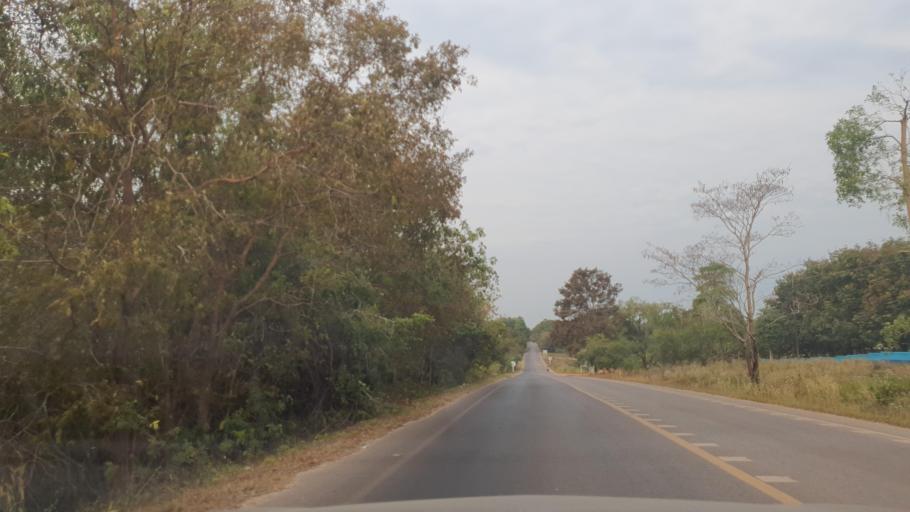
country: TH
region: Changwat Bueng Kan
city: Bung Khla
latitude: 18.2395
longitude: 104.0235
